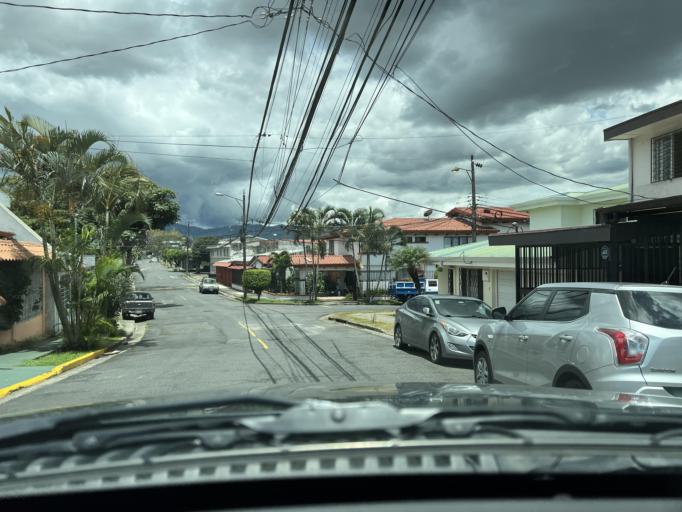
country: CR
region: San Jose
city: San Pedro
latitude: 9.9249
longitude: -84.0630
